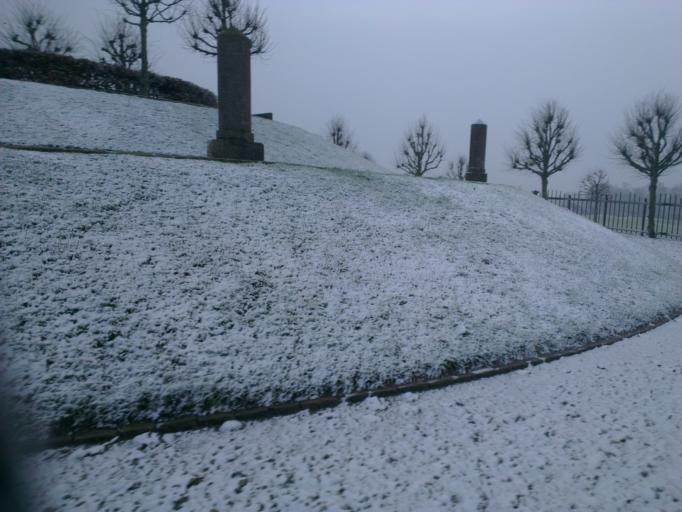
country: DK
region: Capital Region
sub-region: Frederikssund Kommune
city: Jaegerspris
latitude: 55.8610
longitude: 11.9675
